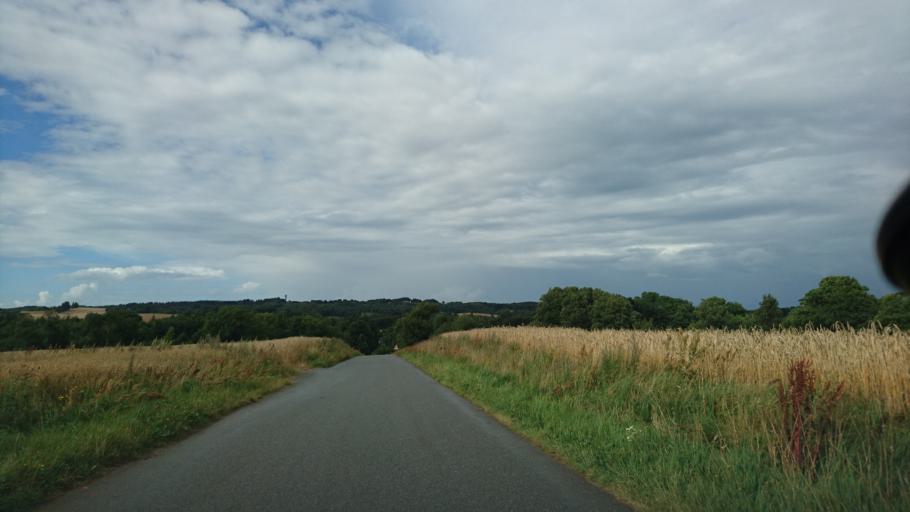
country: DK
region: North Denmark
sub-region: Frederikshavn Kommune
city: Frederikshavn
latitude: 57.3961
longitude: 10.4780
